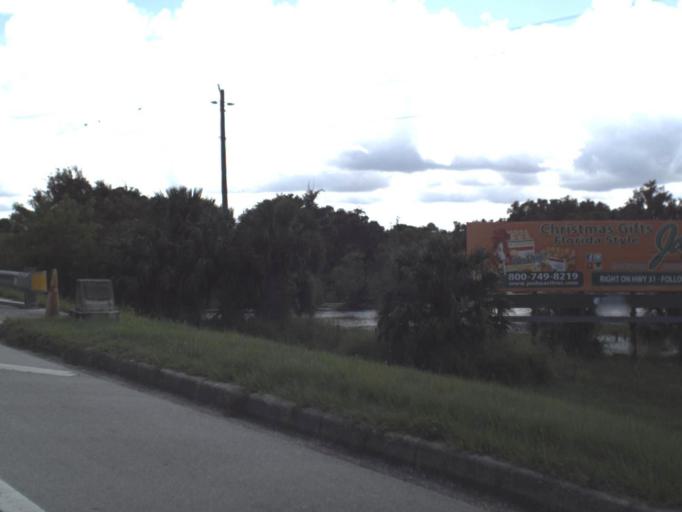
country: US
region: Florida
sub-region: DeSoto County
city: Arcadia
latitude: 27.2213
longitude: -81.8773
